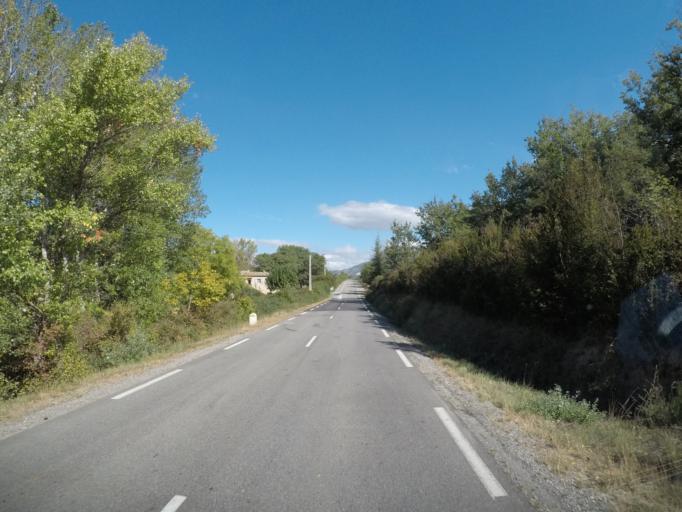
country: FR
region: Provence-Alpes-Cote d'Azur
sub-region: Departement des Alpes-de-Haute-Provence
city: Mallemoisson
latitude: 43.9690
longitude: 6.1915
